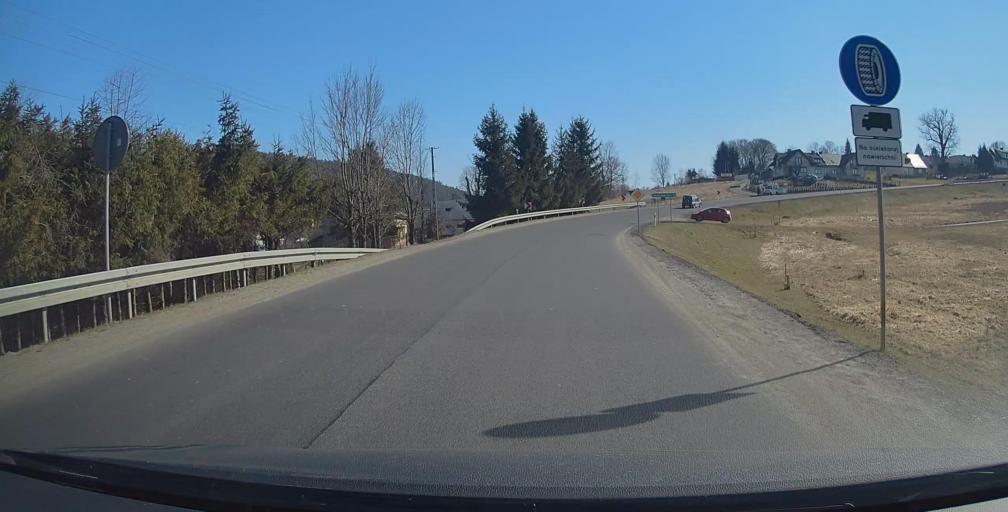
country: PL
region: Subcarpathian Voivodeship
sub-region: Powiat przemyski
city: Bircza
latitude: 49.6625
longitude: 22.4334
